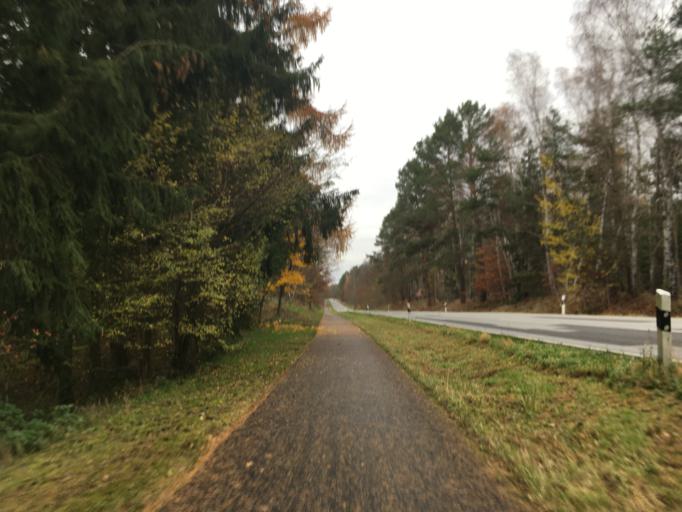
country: DE
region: Brandenburg
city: Mullrose
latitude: 52.2211
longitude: 14.4444
